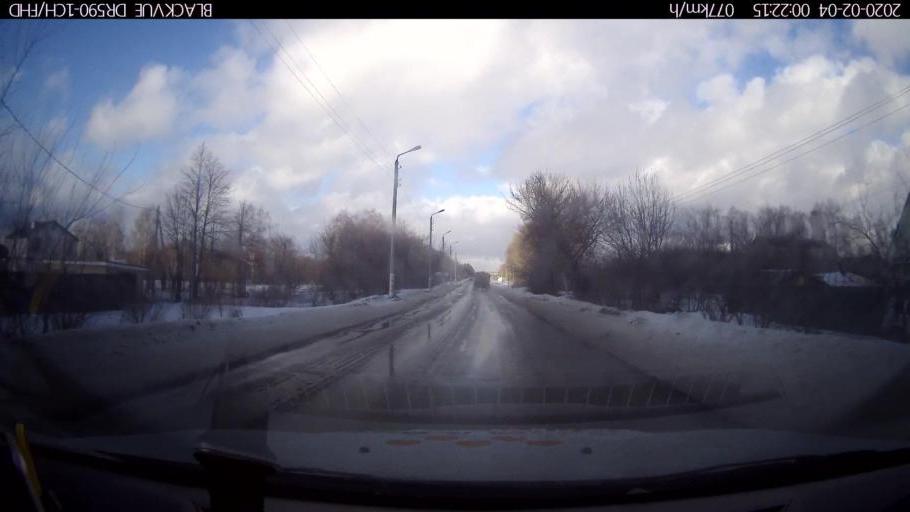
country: RU
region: Nizjnij Novgorod
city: Kstovo
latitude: 55.9702
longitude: 44.2103
